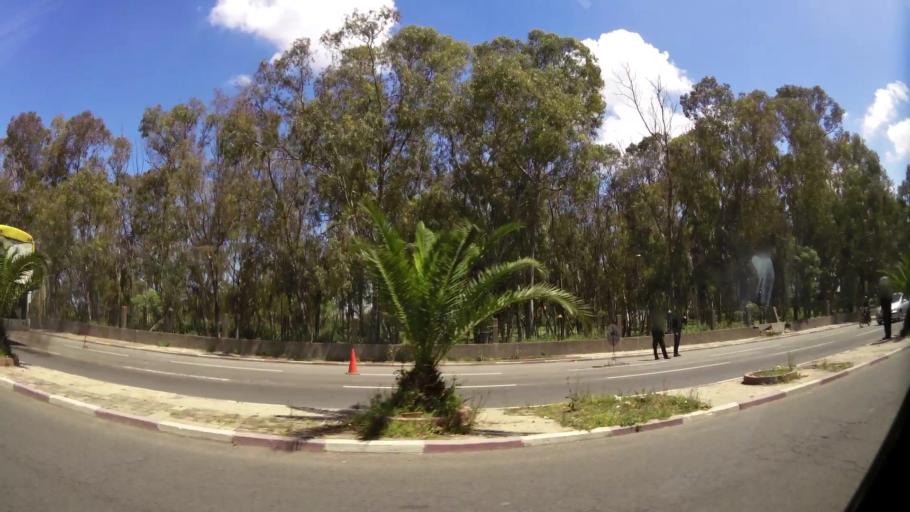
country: MA
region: Grand Casablanca
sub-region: Casablanca
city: Casablanca
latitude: 33.5647
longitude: -7.5780
